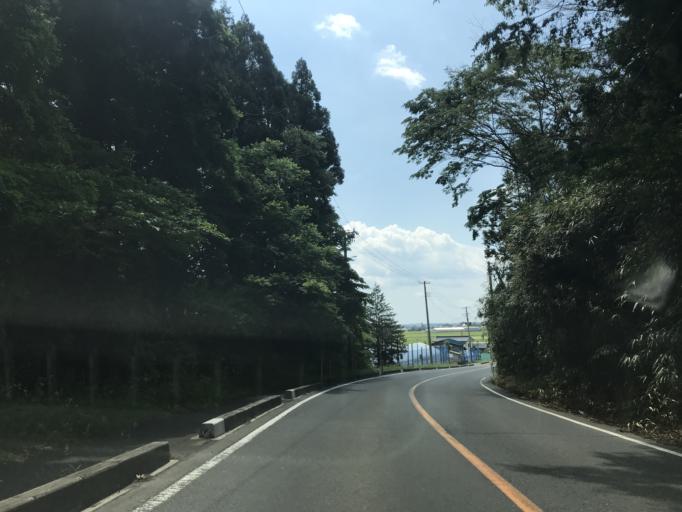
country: JP
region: Miyagi
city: Kogota
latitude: 38.6190
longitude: 141.0184
